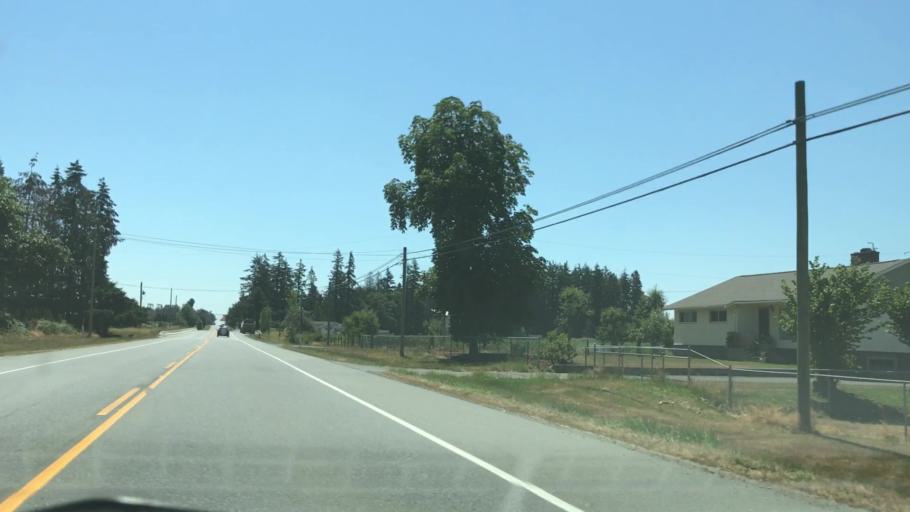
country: CA
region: British Columbia
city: Aldergrove
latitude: 49.0394
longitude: -122.4926
